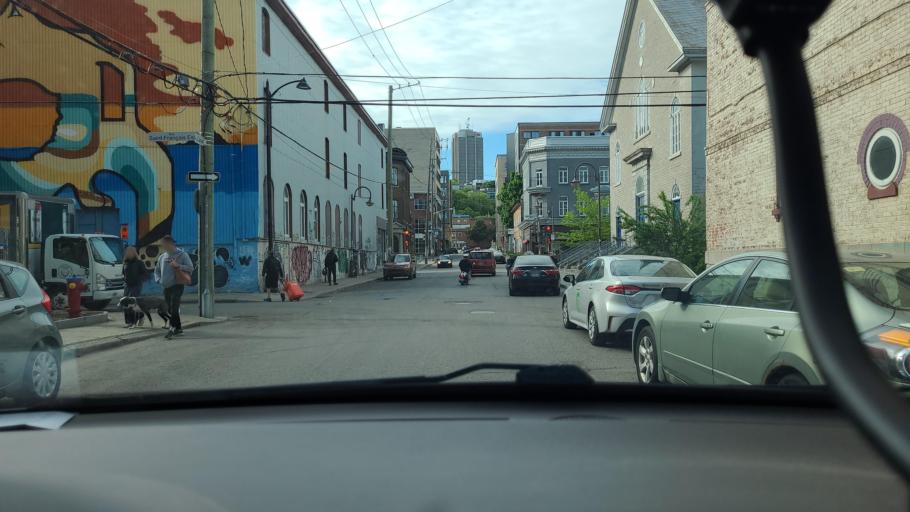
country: CA
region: Quebec
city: Quebec
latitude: 46.8135
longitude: -71.2289
